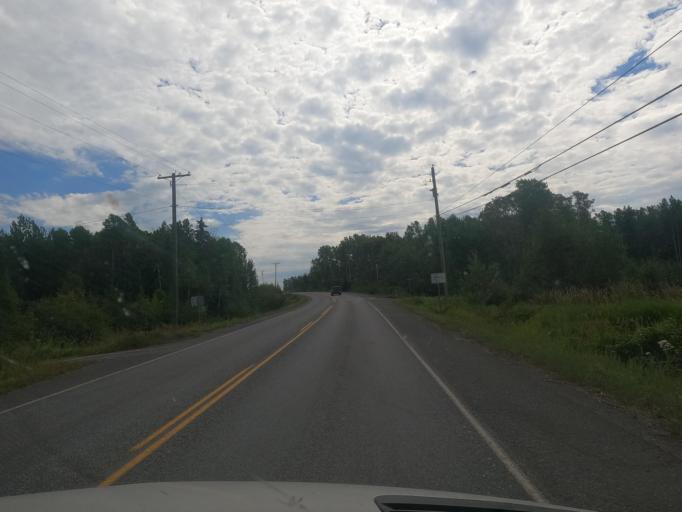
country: CA
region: British Columbia
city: Smithers
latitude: 54.8542
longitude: -127.2253
